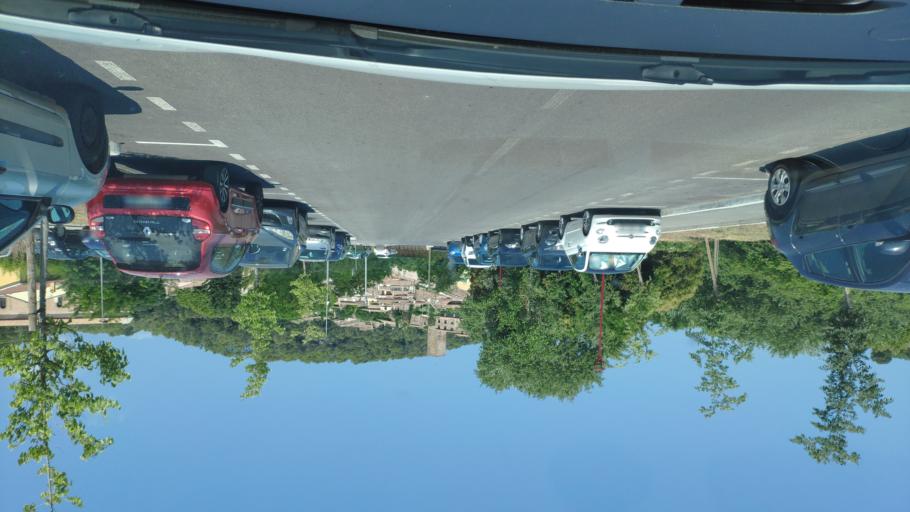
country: FR
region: Provence-Alpes-Cote d'Azur
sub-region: Departement du Var
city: Les Arcs
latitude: 43.4623
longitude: 6.4809
